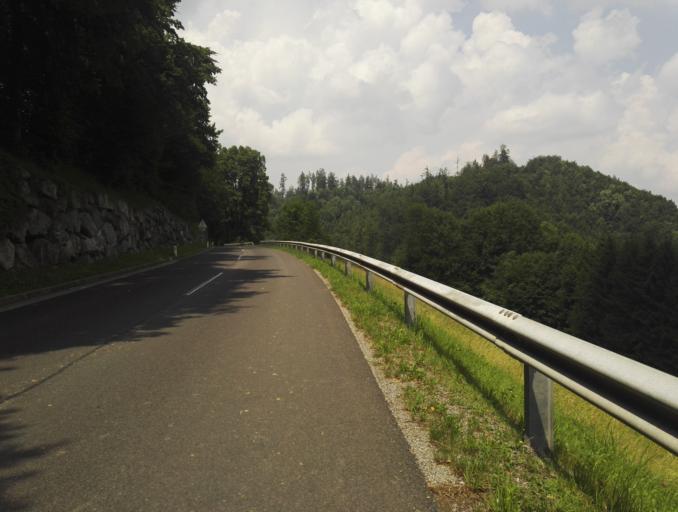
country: AT
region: Styria
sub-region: Politischer Bezirk Graz-Umgebung
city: Gratwein
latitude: 47.0879
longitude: 15.3141
